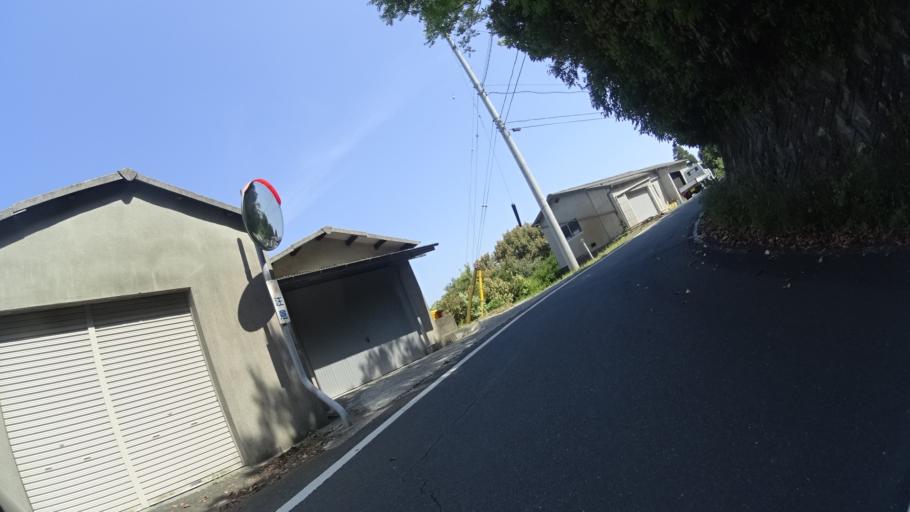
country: JP
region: Ehime
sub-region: Nishiuwa-gun
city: Ikata-cho
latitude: 33.3743
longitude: 132.0560
